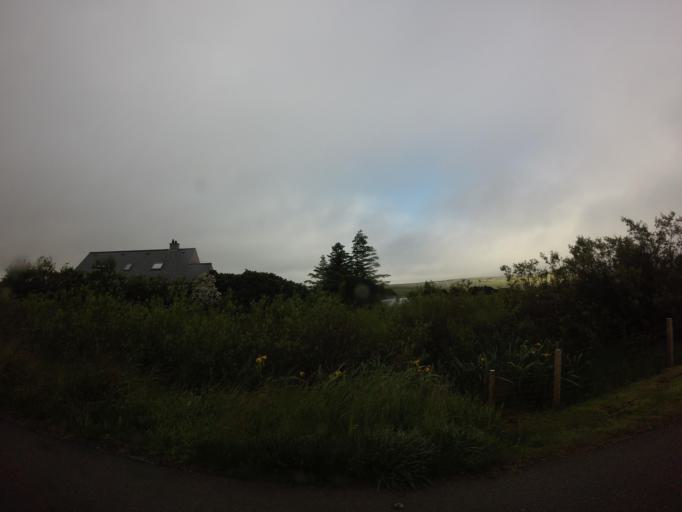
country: GB
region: Scotland
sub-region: Eilean Siar
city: Stornoway
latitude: 58.1946
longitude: -6.2224
